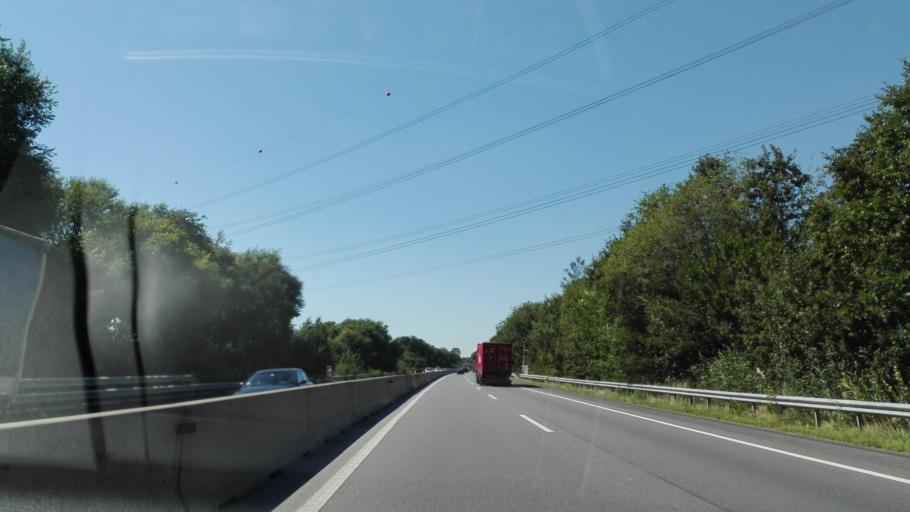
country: AT
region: Lower Austria
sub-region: Politischer Bezirk Bruck an der Leitha
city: Bruck an der Leitha
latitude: 48.0454
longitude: 16.7493
